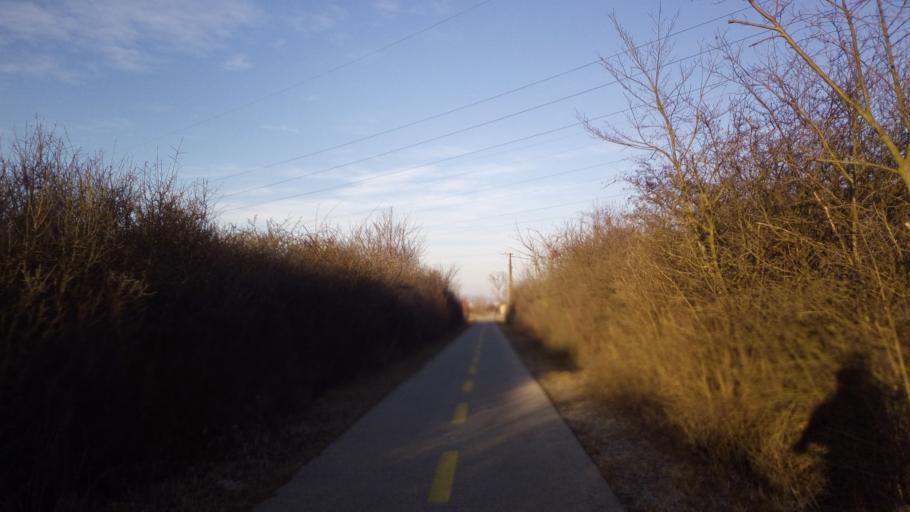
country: HU
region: Baranya
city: Pellerd
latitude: 46.0470
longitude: 18.1903
